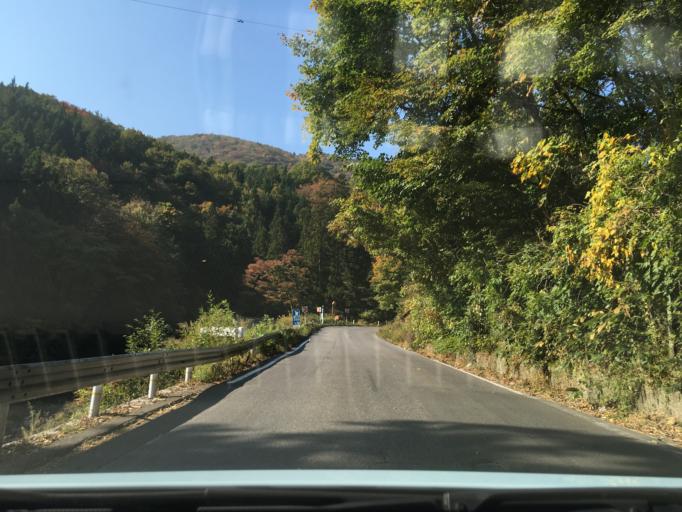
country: JP
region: Fukushima
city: Sukagawa
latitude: 37.3056
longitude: 140.1479
